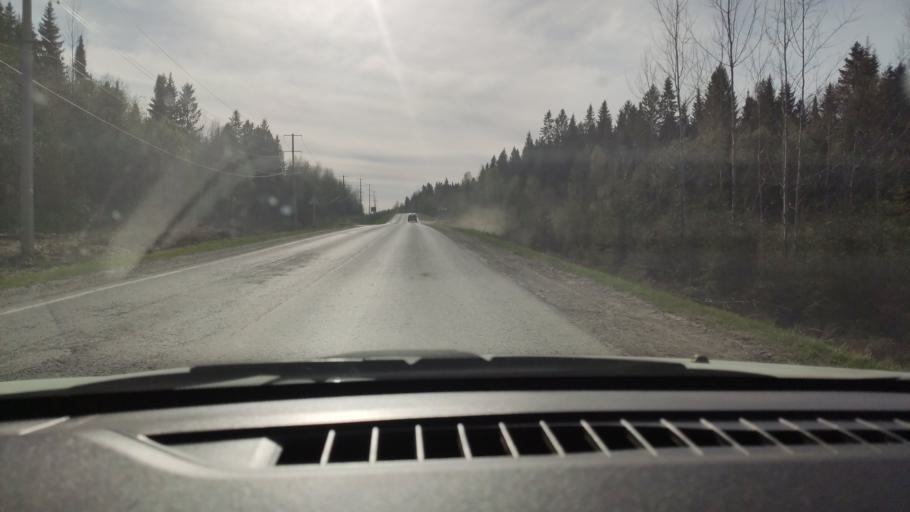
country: RU
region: Perm
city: Novyye Lyady
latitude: 57.9408
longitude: 56.6080
